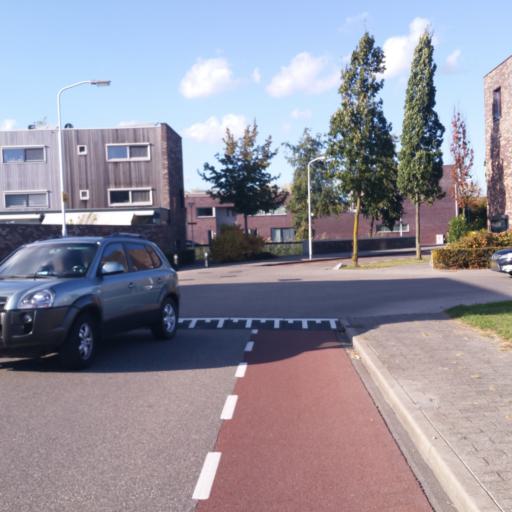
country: NL
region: Utrecht
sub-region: Gemeente IJsselstein
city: IJsselstein
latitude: 52.0089
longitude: 5.0367
